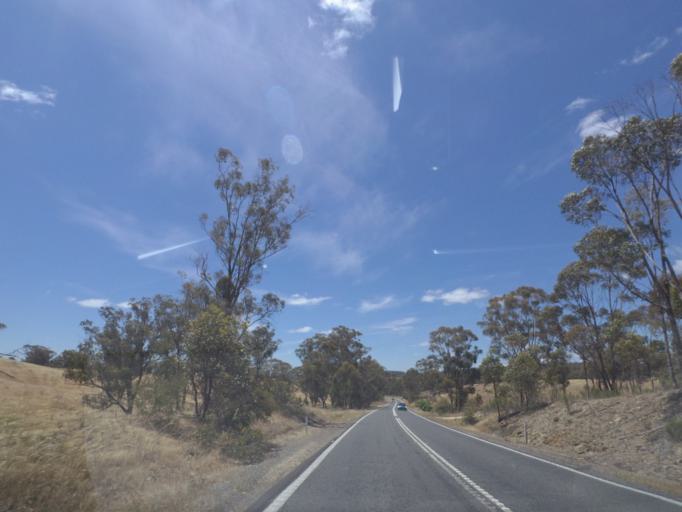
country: AU
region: Victoria
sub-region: Mount Alexander
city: Castlemaine
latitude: -37.2028
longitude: 144.1425
